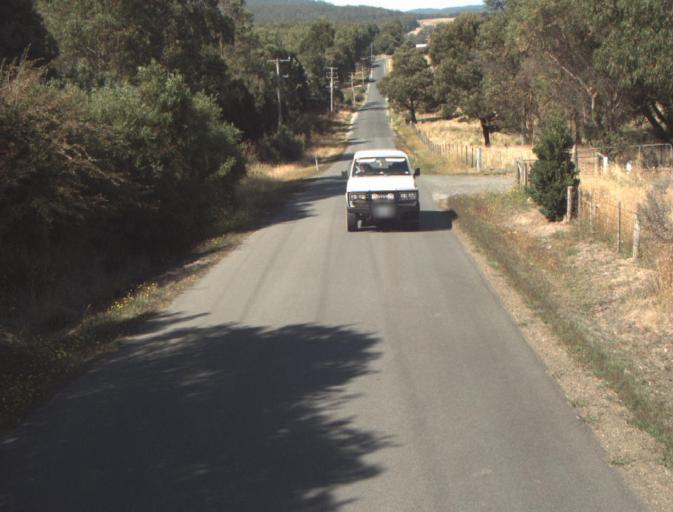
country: AU
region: Tasmania
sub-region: Launceston
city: Mayfield
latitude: -41.2360
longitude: 147.2343
